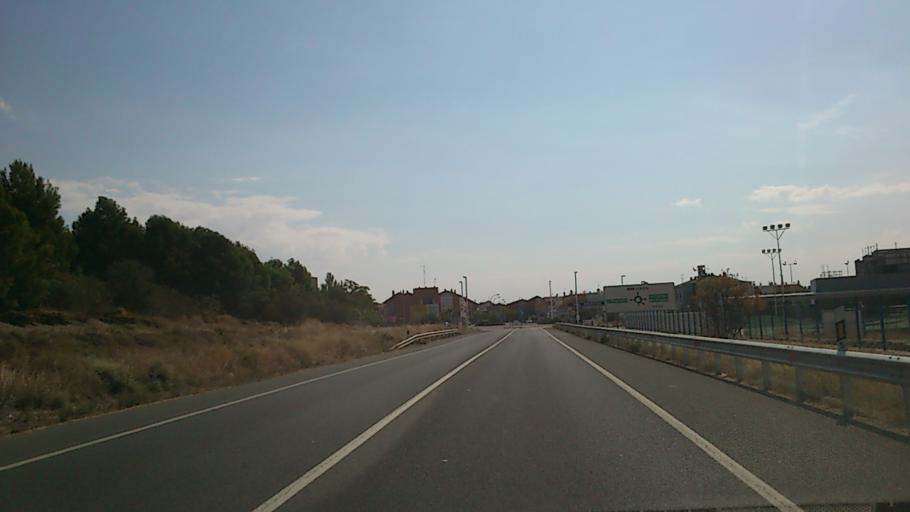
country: ES
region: Aragon
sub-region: Provincia de Zaragoza
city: Puebla de Alfinden
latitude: 41.6352
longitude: -0.7592
